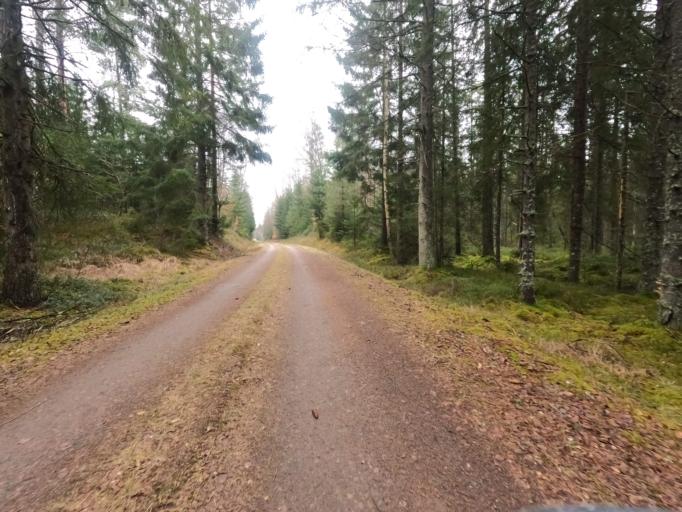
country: SE
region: Kronoberg
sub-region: Markaryds Kommun
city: Stromsnasbruk
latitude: 56.7889
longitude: 13.6316
